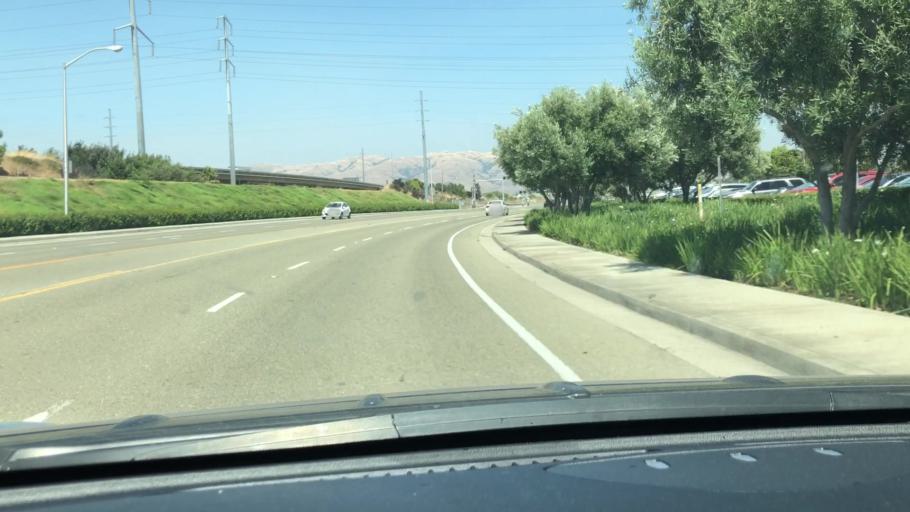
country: US
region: California
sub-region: Santa Clara County
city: Santa Clara
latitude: 37.4157
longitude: -121.9750
